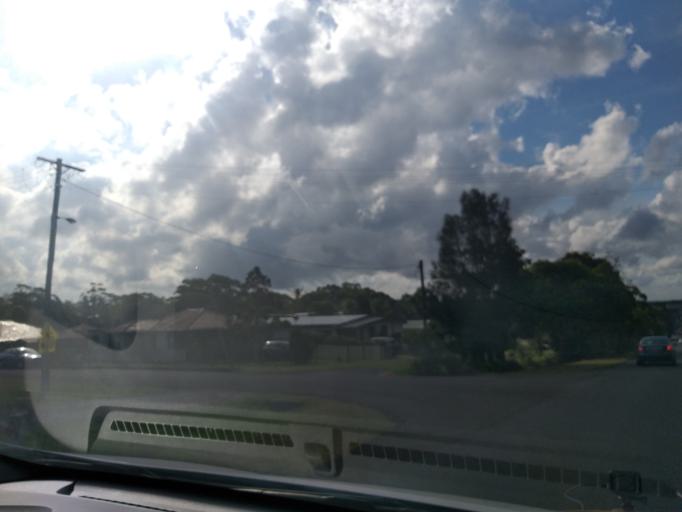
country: AU
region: New South Wales
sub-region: Wollongong
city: Helensburgh
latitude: -34.1984
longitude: 150.9806
